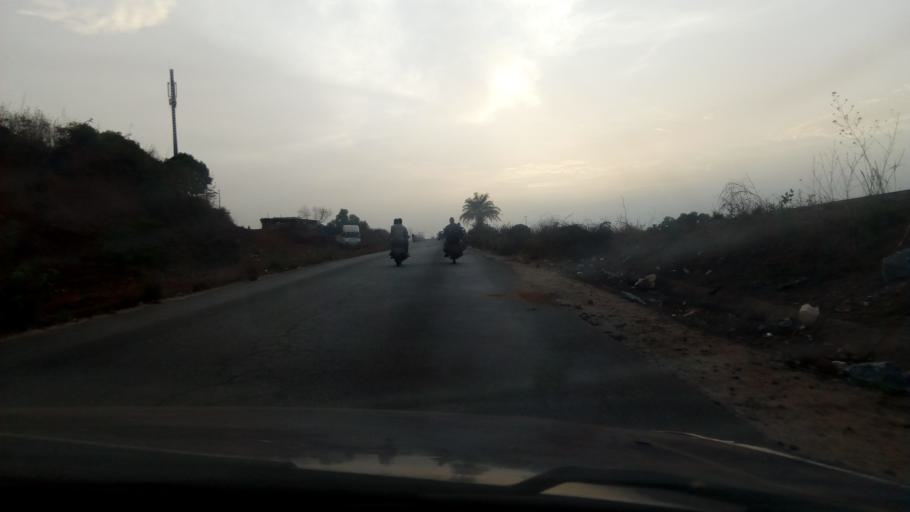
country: GN
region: Kindia
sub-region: Prefecture de Dubreka
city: Dubreka
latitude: 9.7425
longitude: -13.5042
